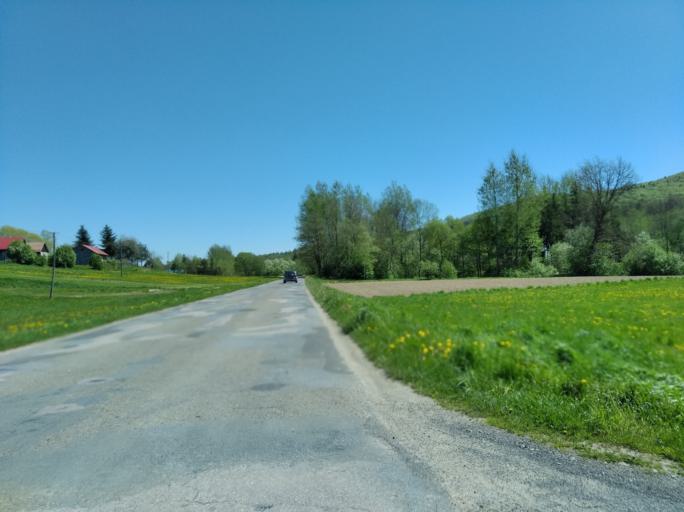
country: PL
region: Subcarpathian Voivodeship
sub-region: Powiat debicki
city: Brzostek
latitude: 49.9165
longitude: 21.4263
